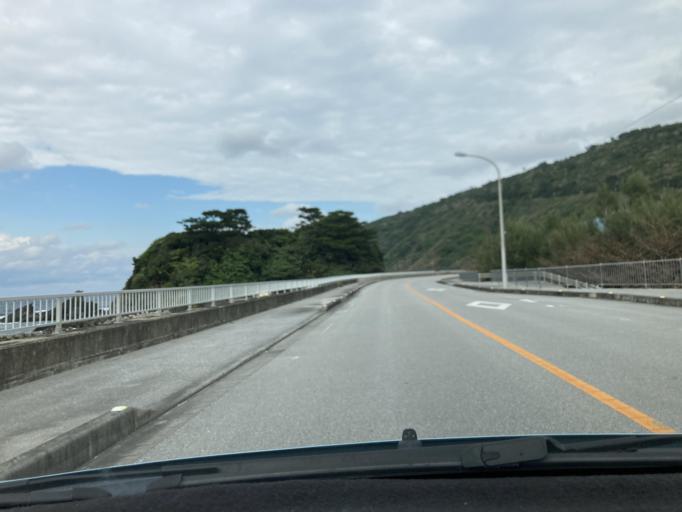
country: JP
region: Okinawa
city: Nago
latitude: 26.7866
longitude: 128.2203
